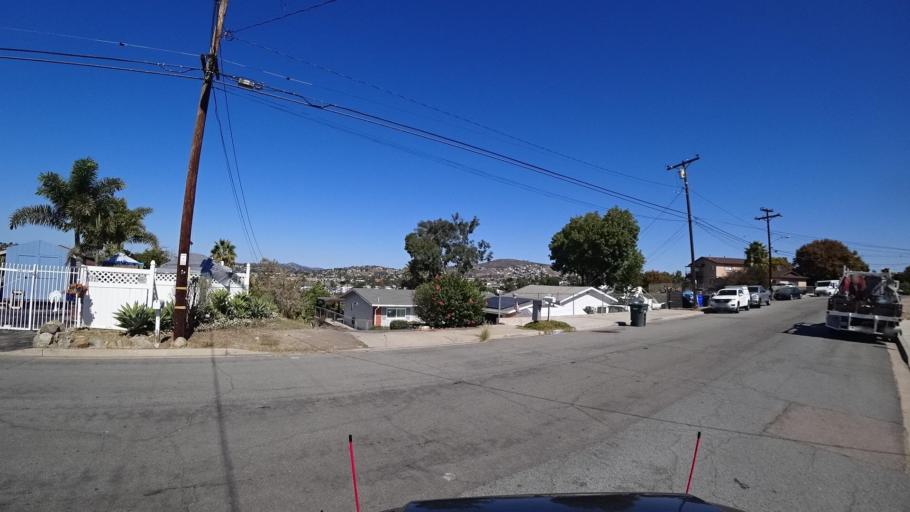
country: US
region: California
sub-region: San Diego County
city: La Presa
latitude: 32.6978
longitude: -117.0078
